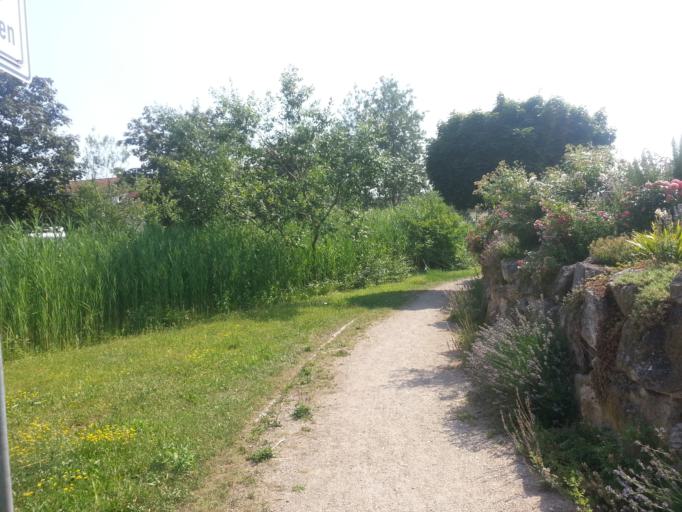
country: DE
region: Baden-Wuerttemberg
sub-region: Karlsruhe Region
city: Ilvesheim
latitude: 49.5006
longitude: 8.5459
